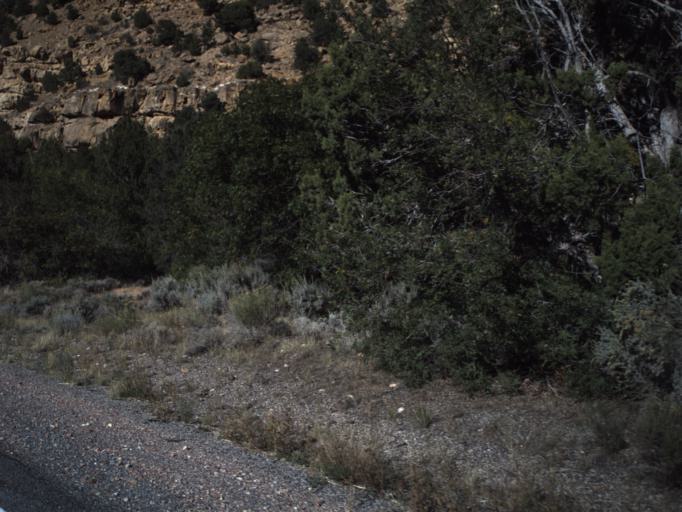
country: US
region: Utah
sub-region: Iron County
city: Parowan
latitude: 37.8190
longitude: -112.8095
